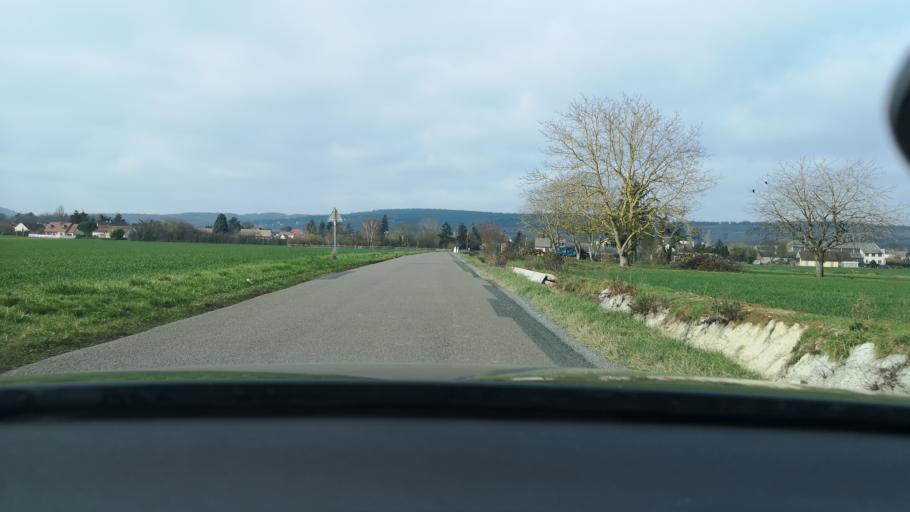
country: FR
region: Bourgogne
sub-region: Departement de Saone-et-Loire
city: Givry
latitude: 46.7781
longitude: 4.7563
